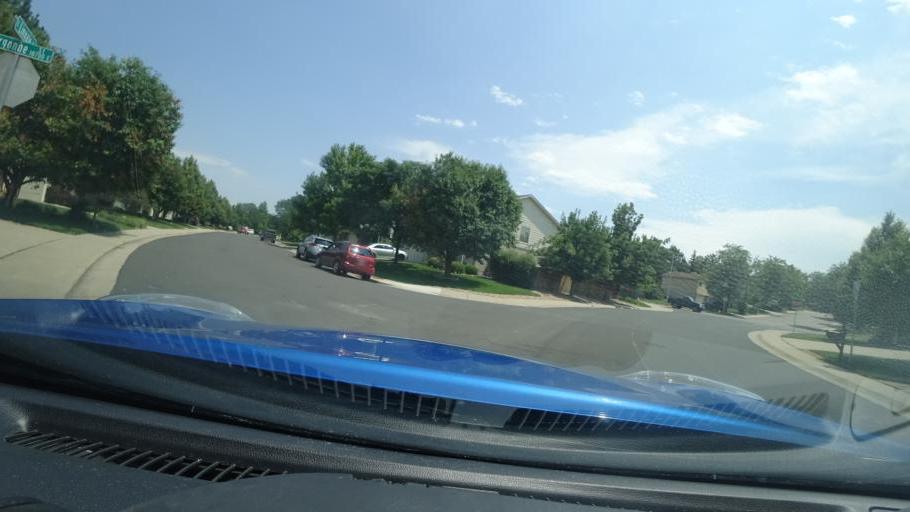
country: US
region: Colorado
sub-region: Adams County
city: Aurora
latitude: 39.6661
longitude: -104.7708
